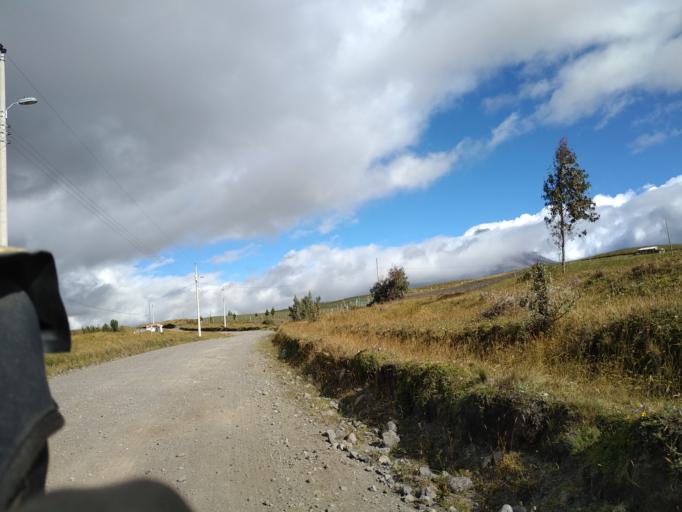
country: EC
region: Pichincha
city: Machachi
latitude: -0.5565
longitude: -78.4544
